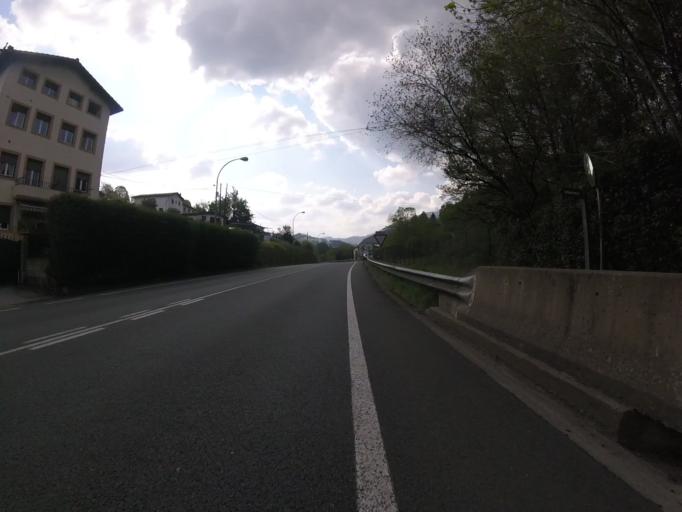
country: ES
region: Basque Country
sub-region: Provincia de Guipuzcoa
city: Azkoitia
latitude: 43.1809
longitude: -2.3193
